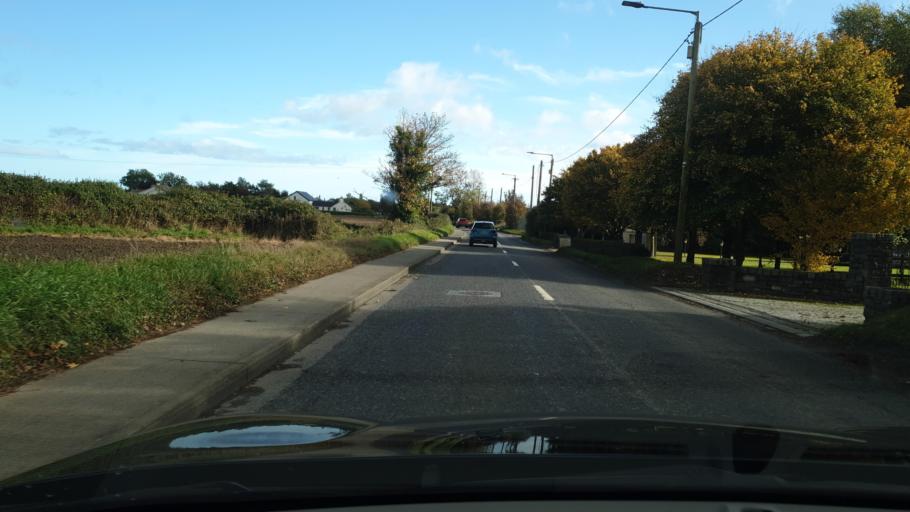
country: IE
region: Leinster
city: Lusk
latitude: 53.5224
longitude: -6.1529
